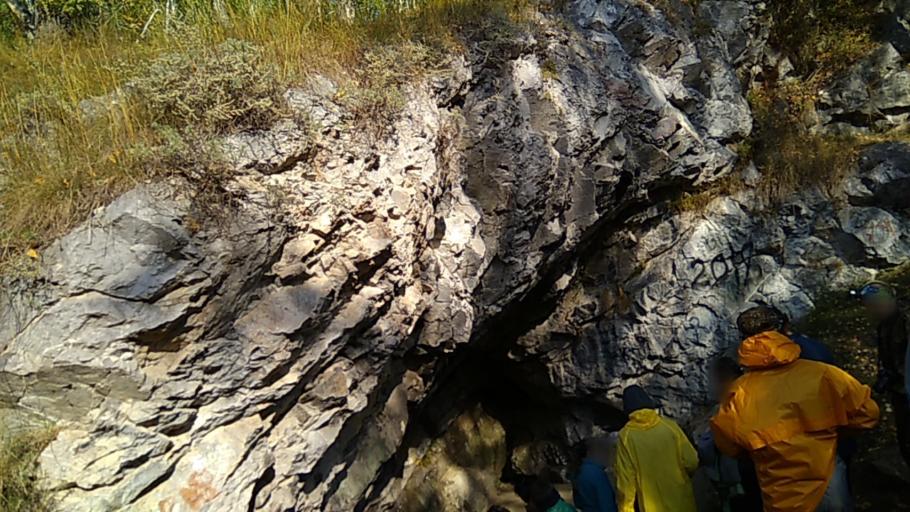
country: RU
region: Sverdlovsk
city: Pokrovskoye
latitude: 56.4290
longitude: 61.6124
